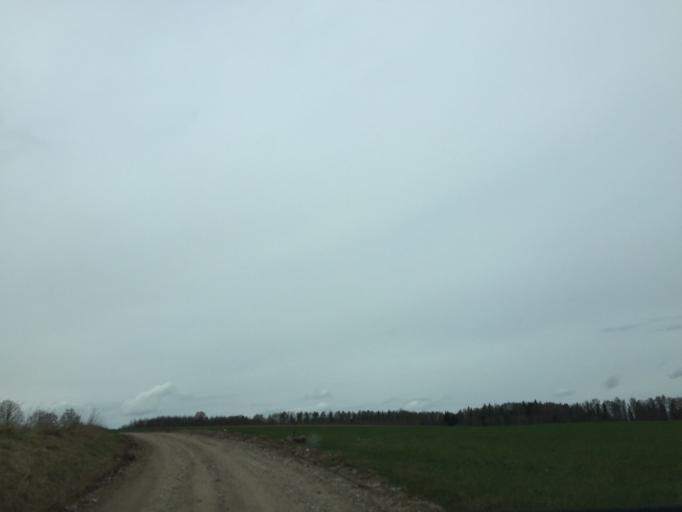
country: LV
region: Priekuli
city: Priekuli
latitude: 57.3327
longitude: 25.3838
